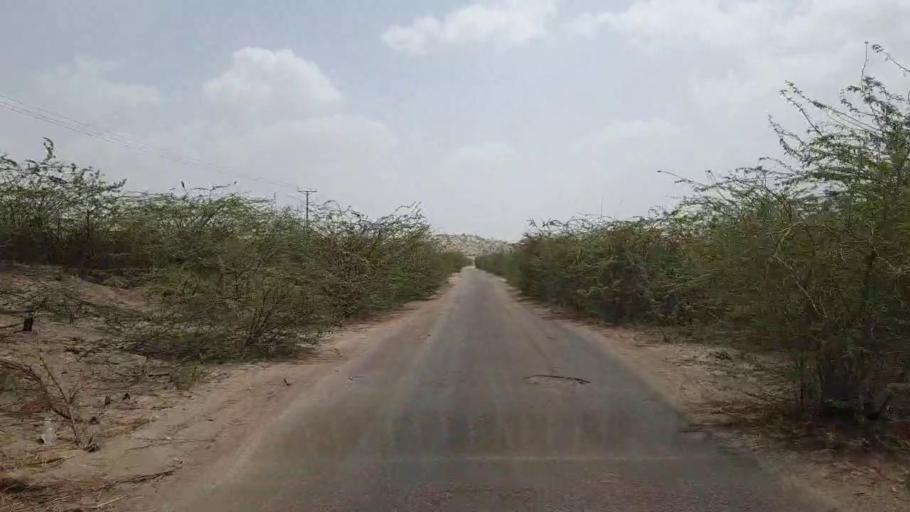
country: PK
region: Sindh
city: Diplo
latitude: 24.3647
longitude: 69.3970
